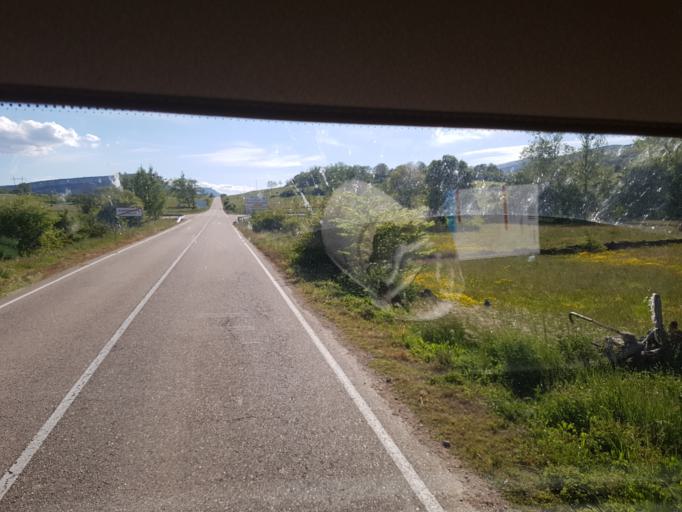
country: ES
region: Castille and Leon
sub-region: Provincia de Burgos
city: Espinosa de los Monteros
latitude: 43.0605
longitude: -3.5945
